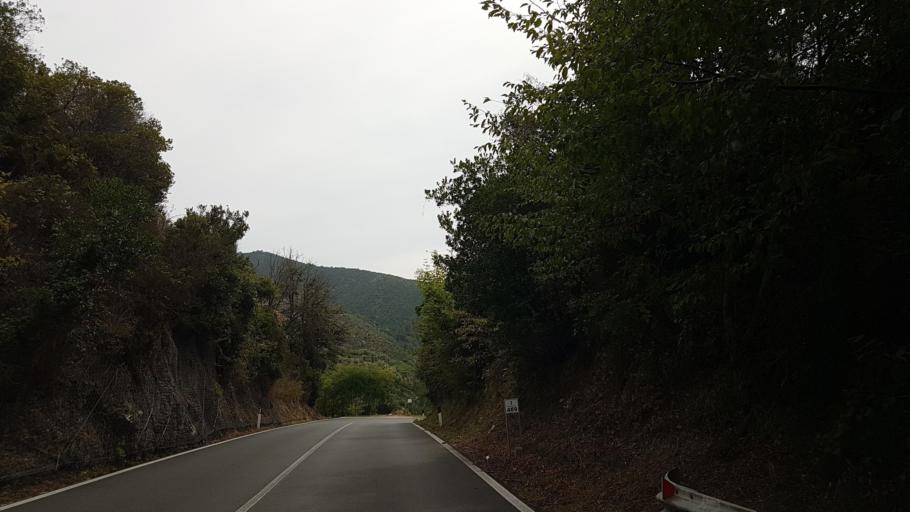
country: IT
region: Liguria
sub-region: Provincia di Genova
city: Casarza Ligure
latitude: 44.2612
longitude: 9.4457
